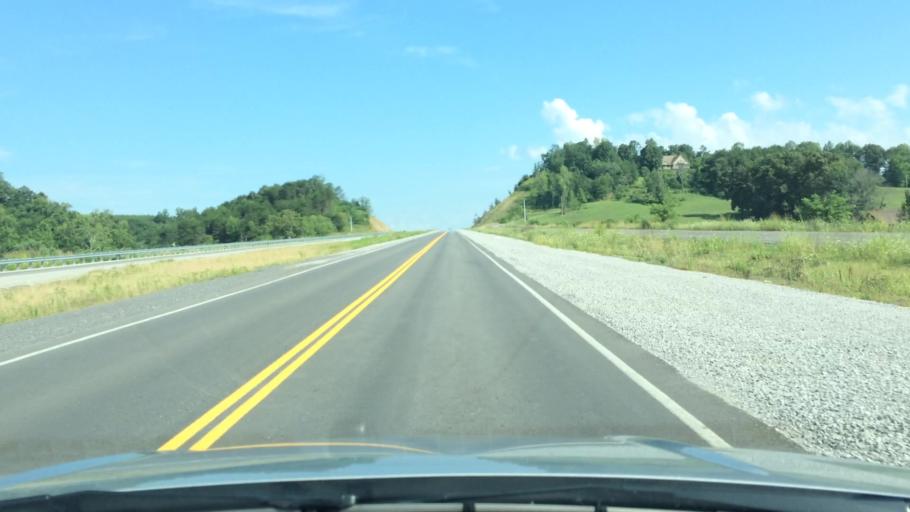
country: US
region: Tennessee
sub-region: Jefferson County
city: White Pine
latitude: 36.1314
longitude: -83.3363
